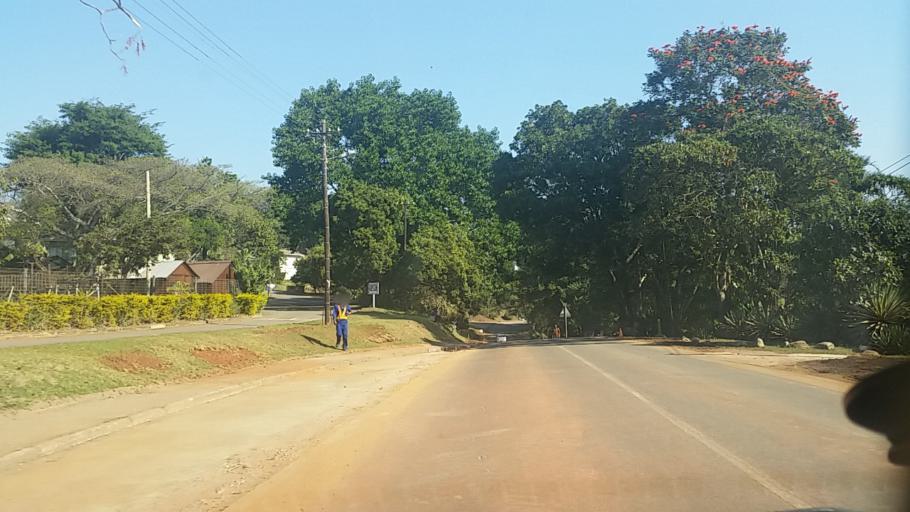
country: ZA
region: KwaZulu-Natal
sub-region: eThekwini Metropolitan Municipality
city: Berea
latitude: -29.8433
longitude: 30.9121
